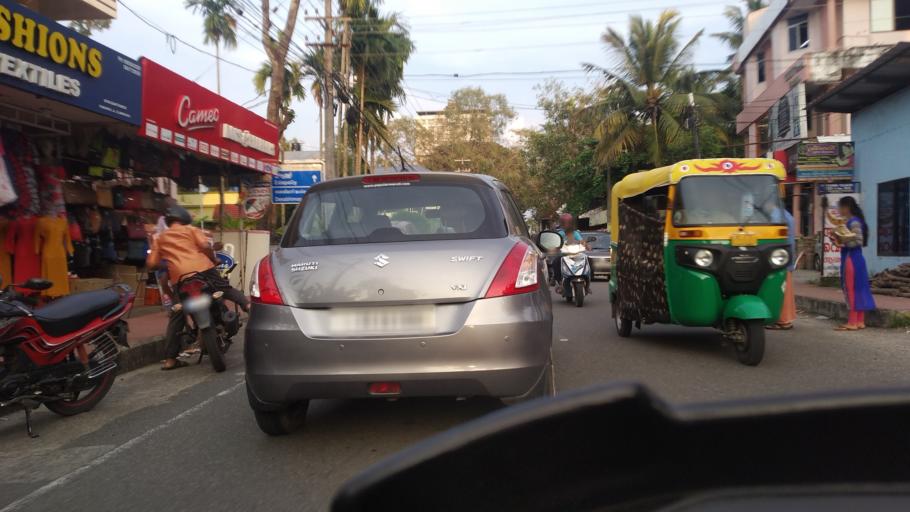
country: IN
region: Kerala
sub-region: Ernakulam
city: Elur
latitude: 10.0192
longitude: 76.2903
